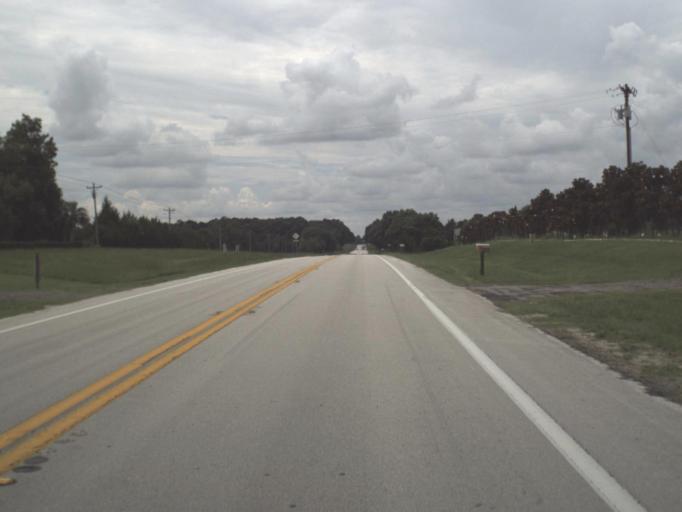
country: US
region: Florida
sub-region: Alachua County
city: High Springs
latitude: 29.7555
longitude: -82.6075
